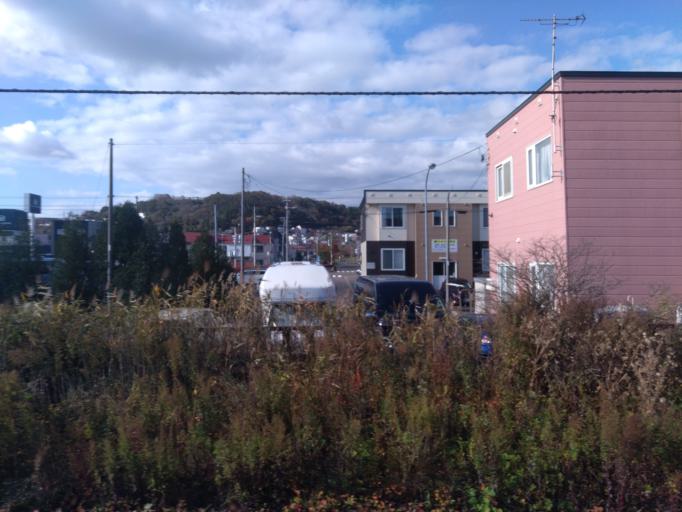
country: JP
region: Hokkaido
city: Muroran
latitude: 42.3556
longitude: 141.0346
